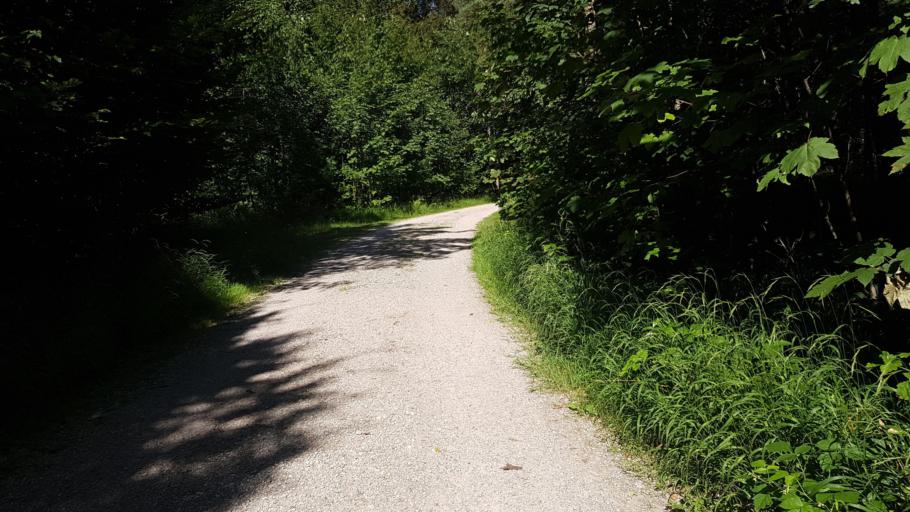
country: DE
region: Bavaria
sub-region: Upper Bavaria
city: Oberschleissheim
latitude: 48.2250
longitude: 11.5724
